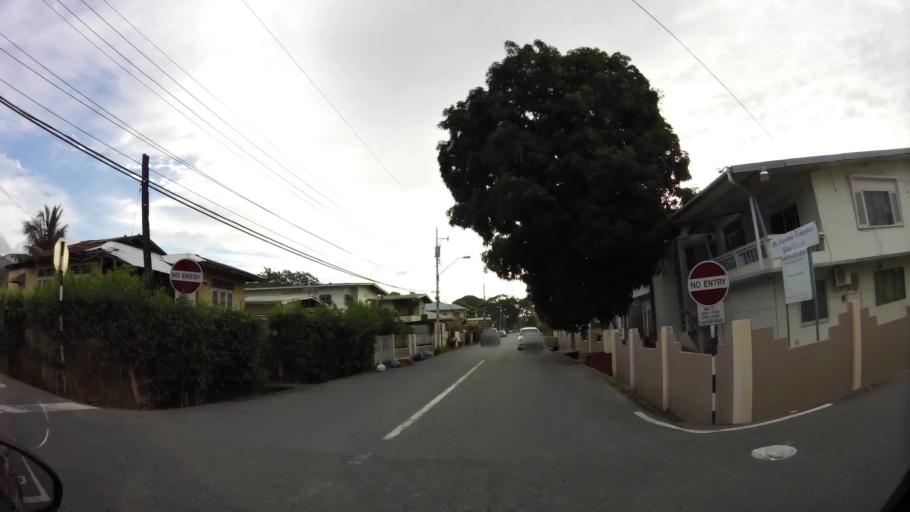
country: TT
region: Tunapuna/Piarco
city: Tunapuna
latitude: 10.6460
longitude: -61.4060
